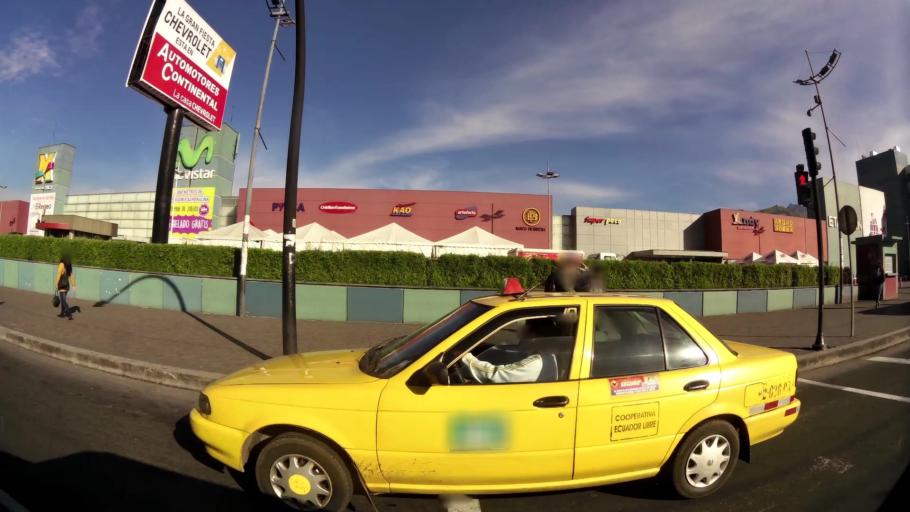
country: EC
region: Pichincha
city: Quito
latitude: -0.2525
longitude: -78.5219
